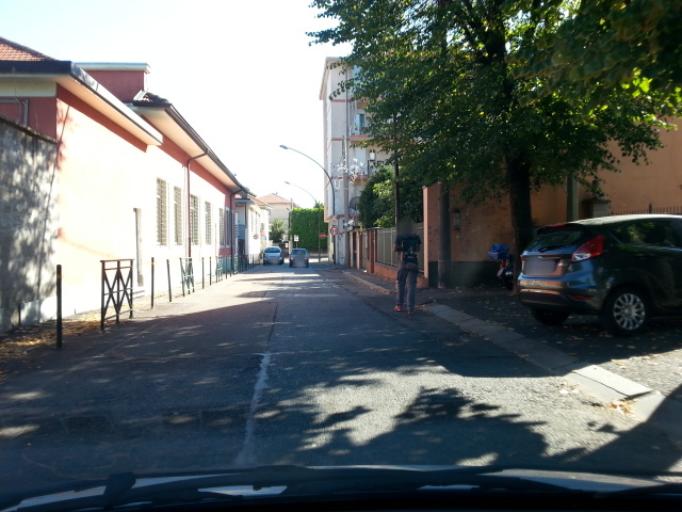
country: IT
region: Piedmont
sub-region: Provincia di Torino
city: Grugliasco
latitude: 45.0622
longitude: 7.5735
